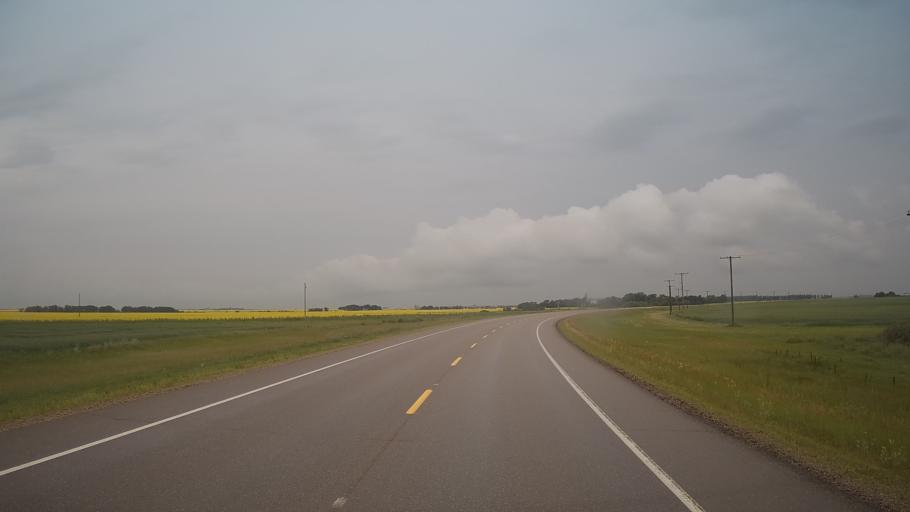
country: CA
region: Saskatchewan
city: Wilkie
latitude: 52.3294
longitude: -108.7114
